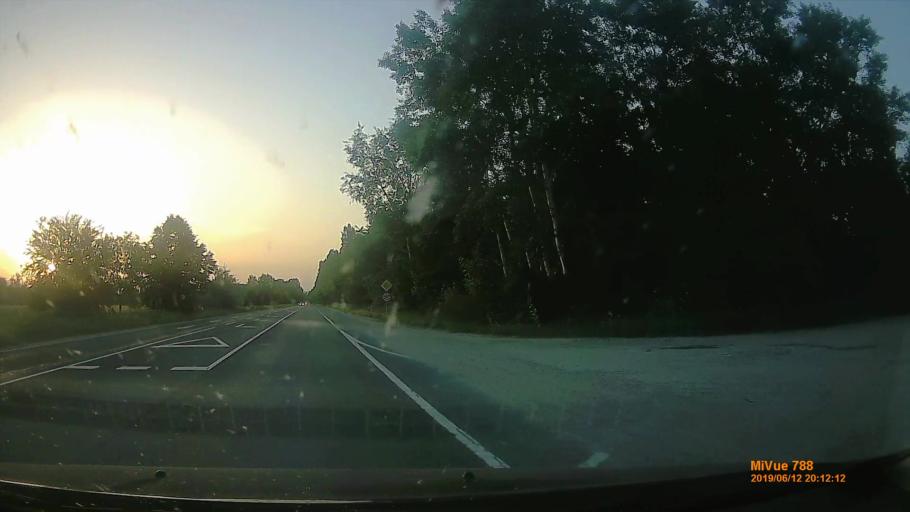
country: HU
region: Pest
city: Ocsa
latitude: 47.2849
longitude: 19.1948
